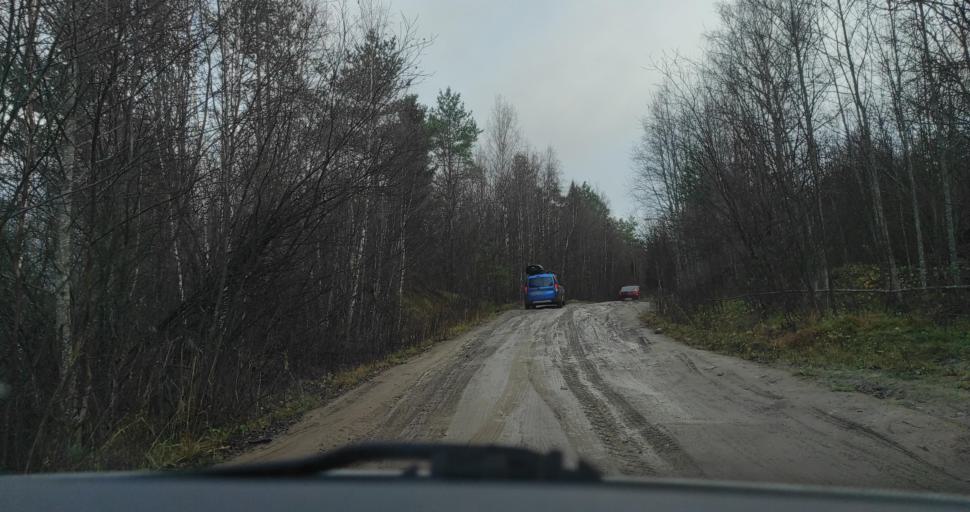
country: RU
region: Republic of Karelia
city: Pitkyaranta
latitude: 61.7360
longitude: 31.3867
